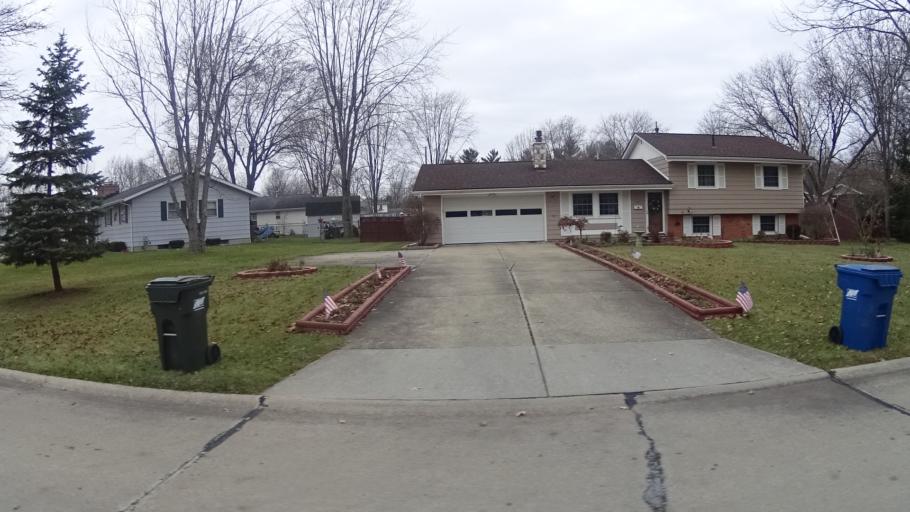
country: US
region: Ohio
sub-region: Lorain County
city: Wellington
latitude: 41.1612
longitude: -82.2108
